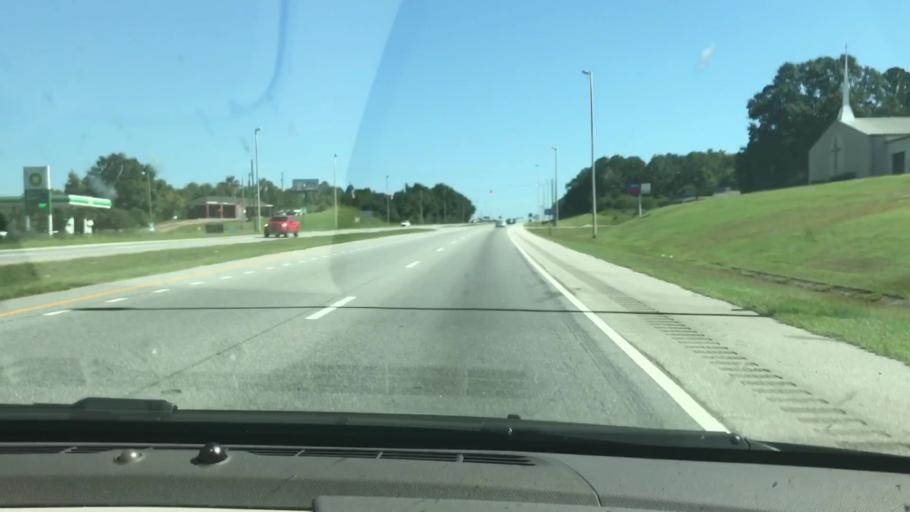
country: US
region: Alabama
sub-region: Russell County
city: Phenix City
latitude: 32.4466
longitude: -85.0178
